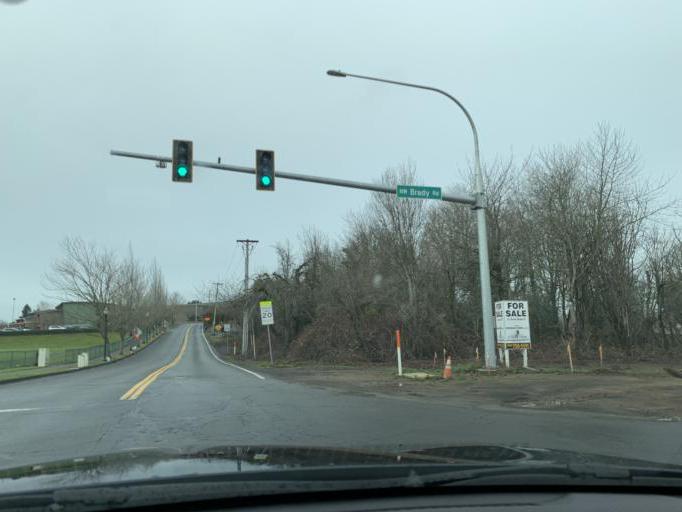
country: US
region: Washington
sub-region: Clark County
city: Camas
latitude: 45.5907
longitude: -122.4527
